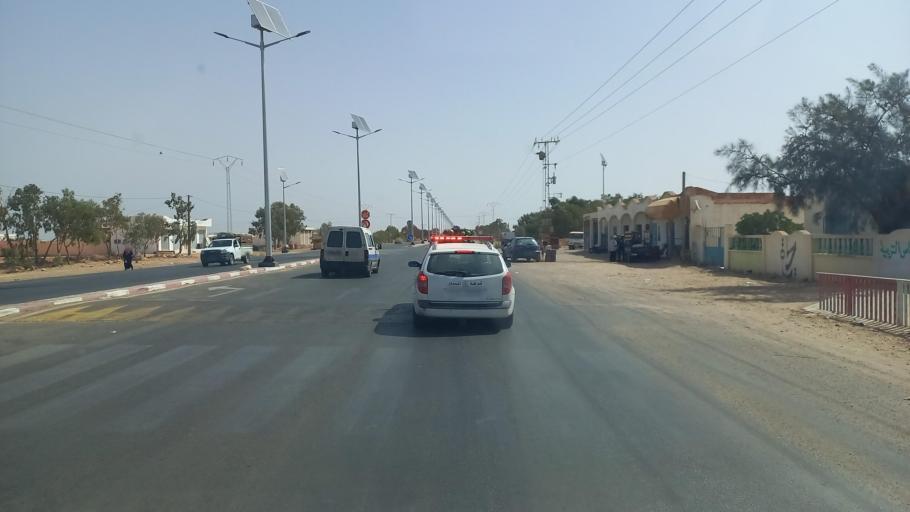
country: TN
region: Madanin
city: Medenine
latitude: 33.3559
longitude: 10.5438
